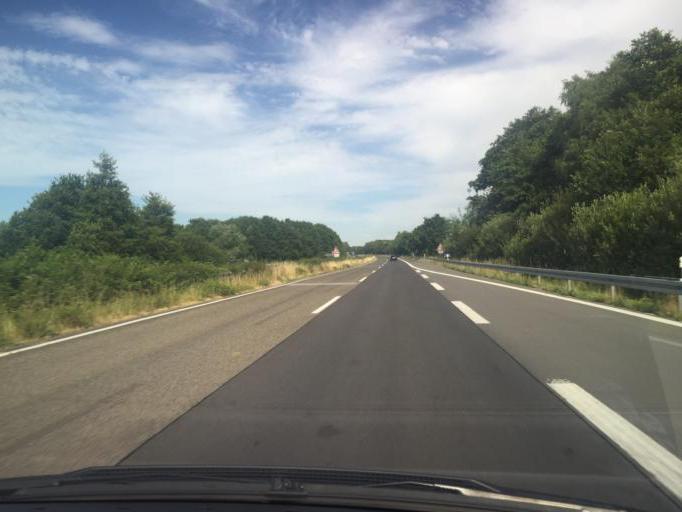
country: DE
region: North Rhine-Westphalia
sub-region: Regierungsbezirk Dusseldorf
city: Uedem
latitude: 51.6369
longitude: 6.2905
